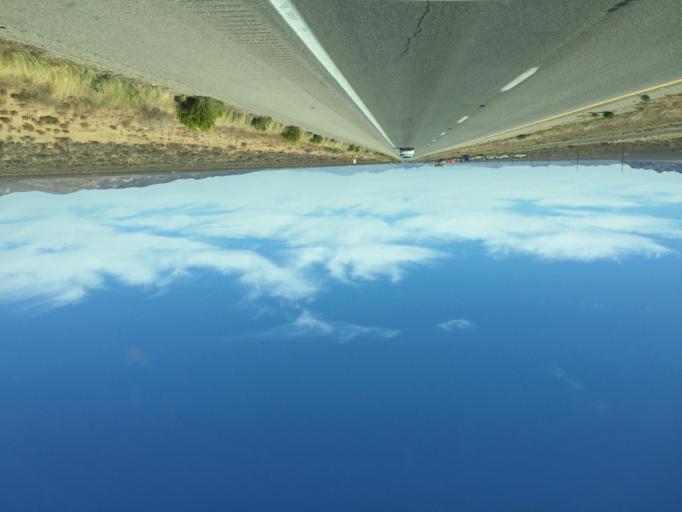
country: US
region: Arizona
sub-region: Mohave County
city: Dolan Springs
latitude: 35.5521
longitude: -114.3677
